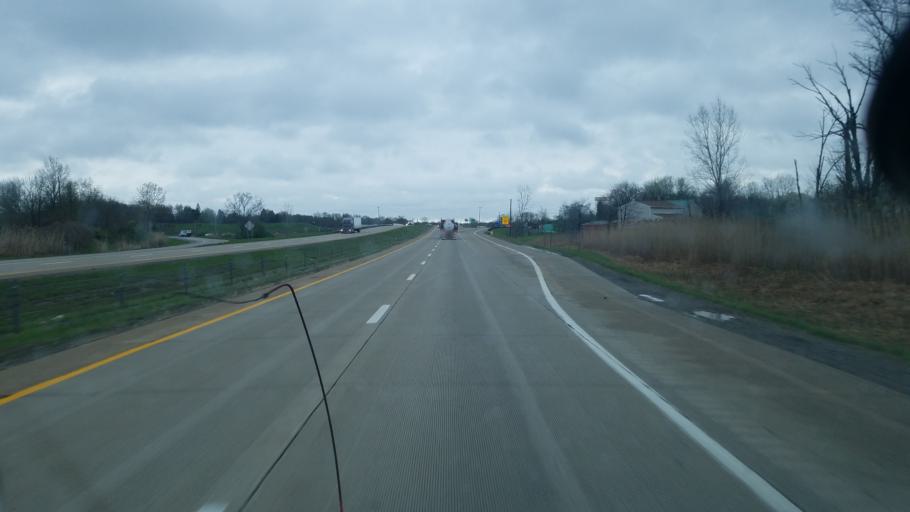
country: US
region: Ohio
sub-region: Portage County
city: Brimfield
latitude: 41.0958
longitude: -81.3810
